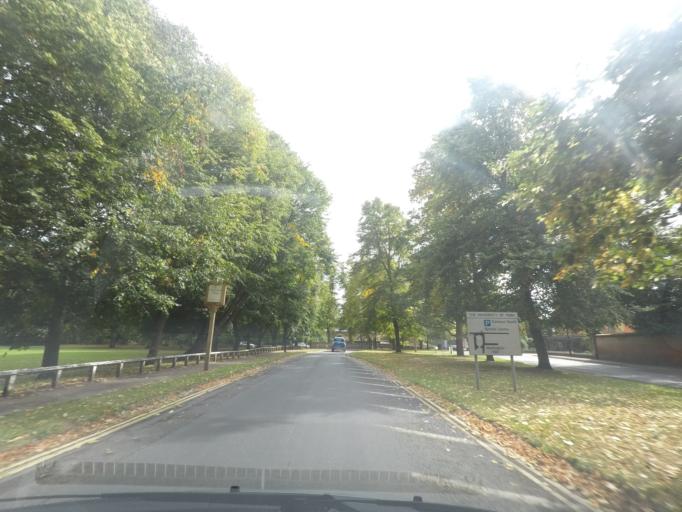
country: GB
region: England
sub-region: City of York
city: Heslington
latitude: 53.9467
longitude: -1.0464
